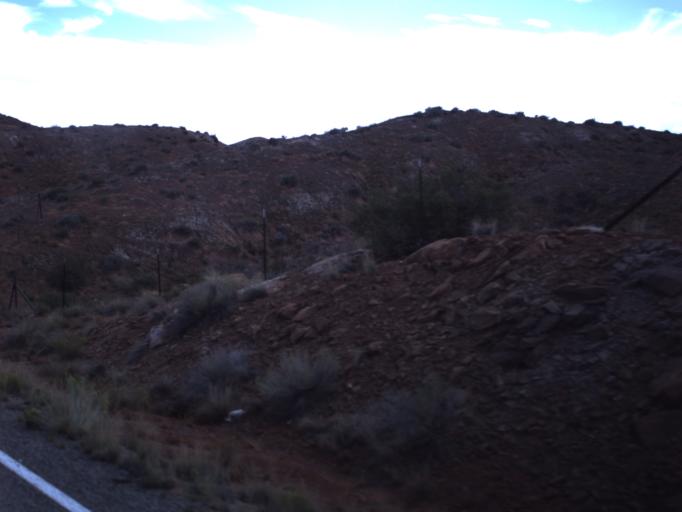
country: US
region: Utah
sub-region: San Juan County
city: Blanding
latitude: 37.2770
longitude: -109.6816
